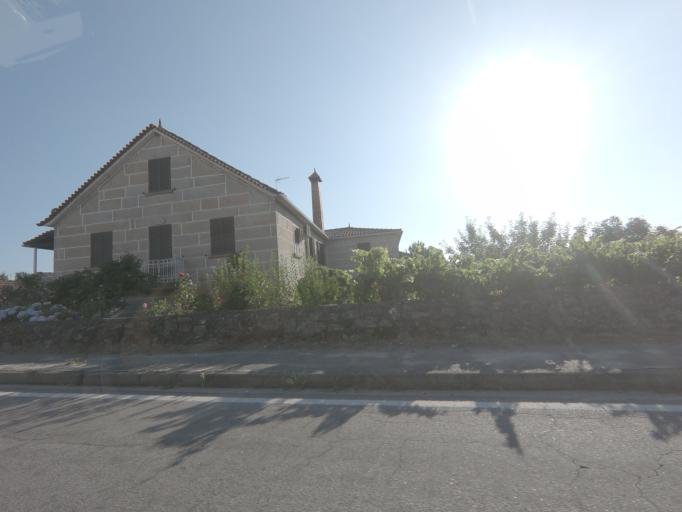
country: PT
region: Vila Real
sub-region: Chaves
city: Chaves
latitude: 41.7924
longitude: -7.4232
